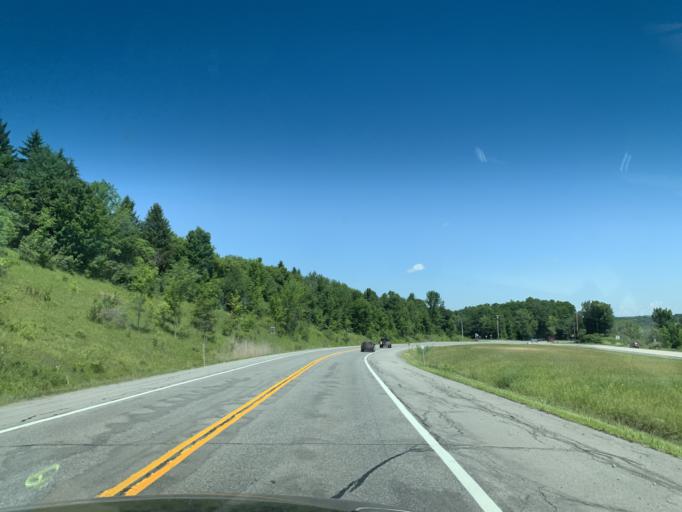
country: US
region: New York
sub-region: Oneida County
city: Chadwicks
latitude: 42.9840
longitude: -75.2536
